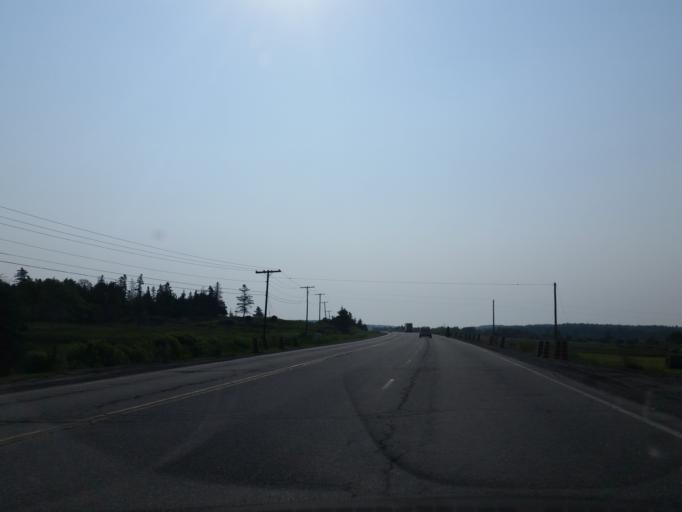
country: CA
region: Ontario
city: Greater Sudbury
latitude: 46.4309
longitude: -80.2495
